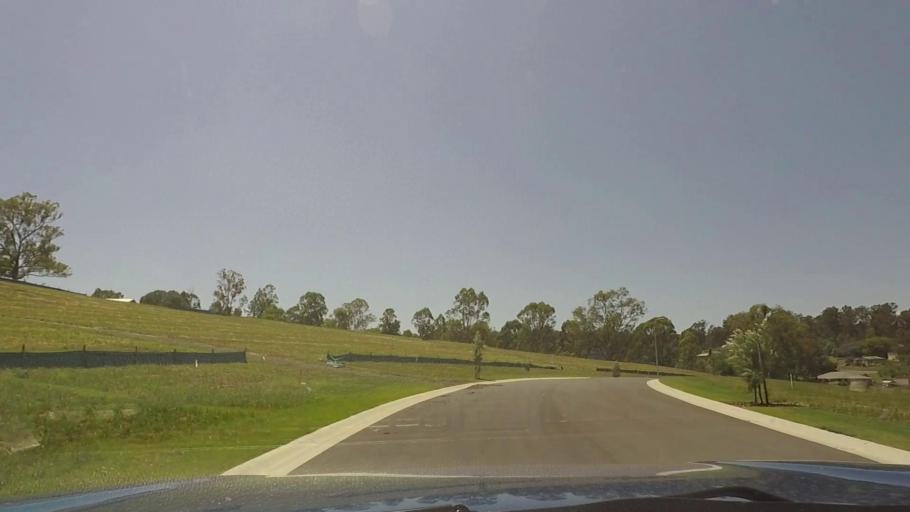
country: AU
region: Queensland
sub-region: Logan
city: Cedar Vale
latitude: -27.8882
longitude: 152.9910
